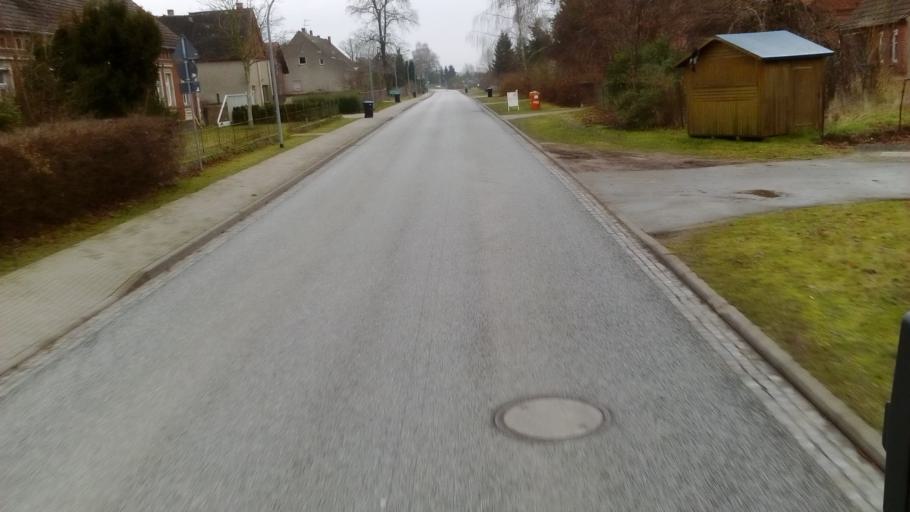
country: DE
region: Brandenburg
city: Pritzwalk
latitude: 53.1398
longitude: 12.2371
